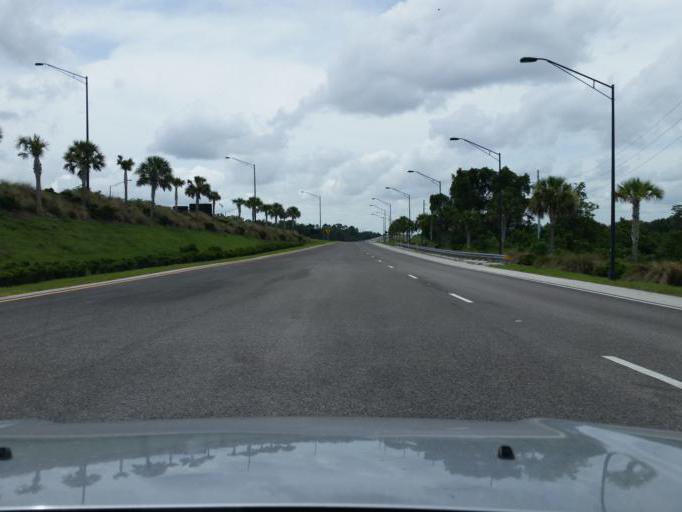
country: US
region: Florida
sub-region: Polk County
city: Citrus Ridge
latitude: 28.3446
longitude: -81.6168
